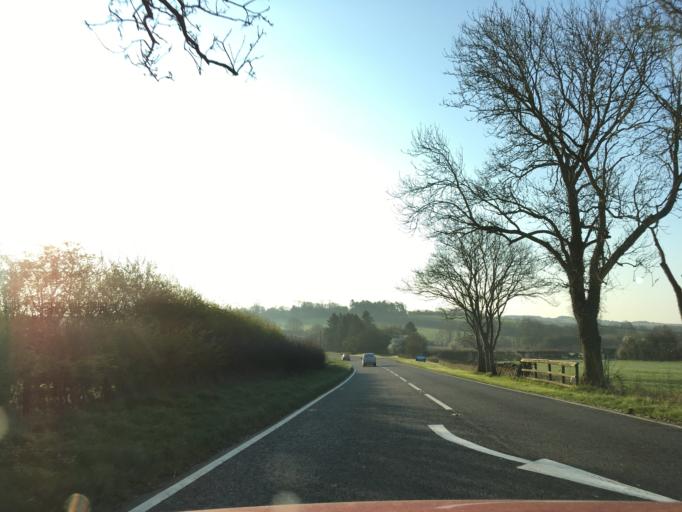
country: GB
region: England
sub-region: Gloucestershire
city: Shipton Village
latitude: 51.8647
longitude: -1.9672
